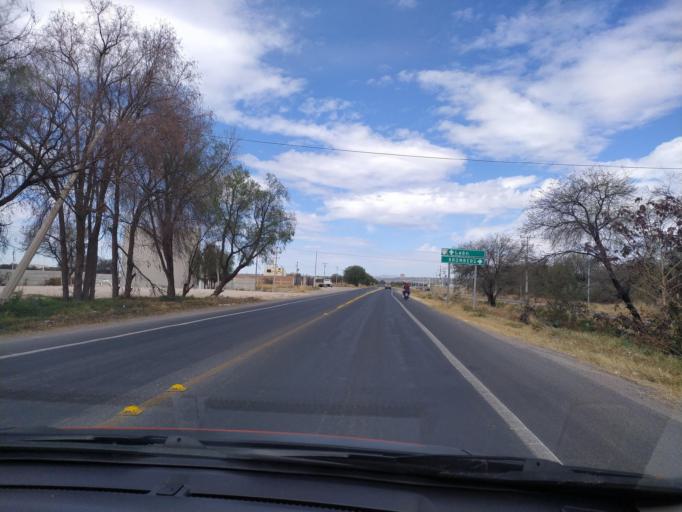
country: LA
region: Oudomxai
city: Muang La
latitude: 21.0009
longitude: 101.8321
